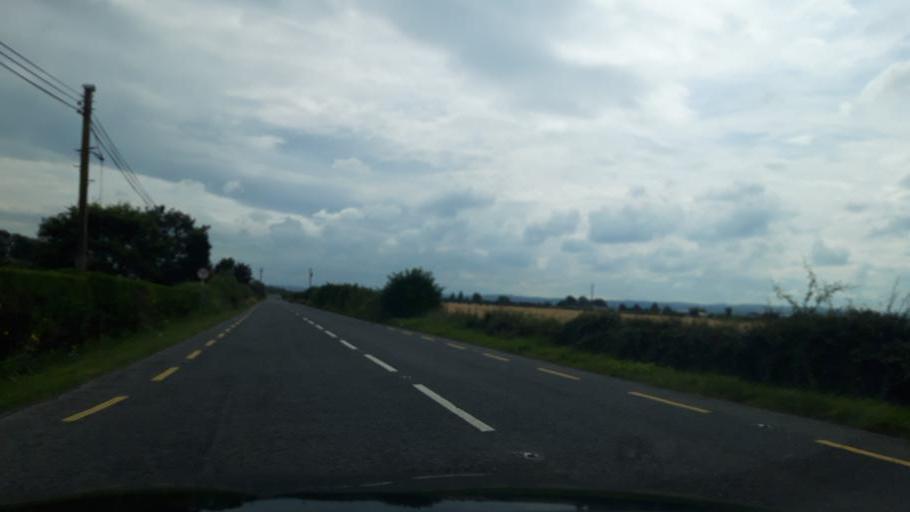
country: IE
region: Leinster
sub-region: Kildare
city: Athy
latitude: 52.9753
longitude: -7.0143
